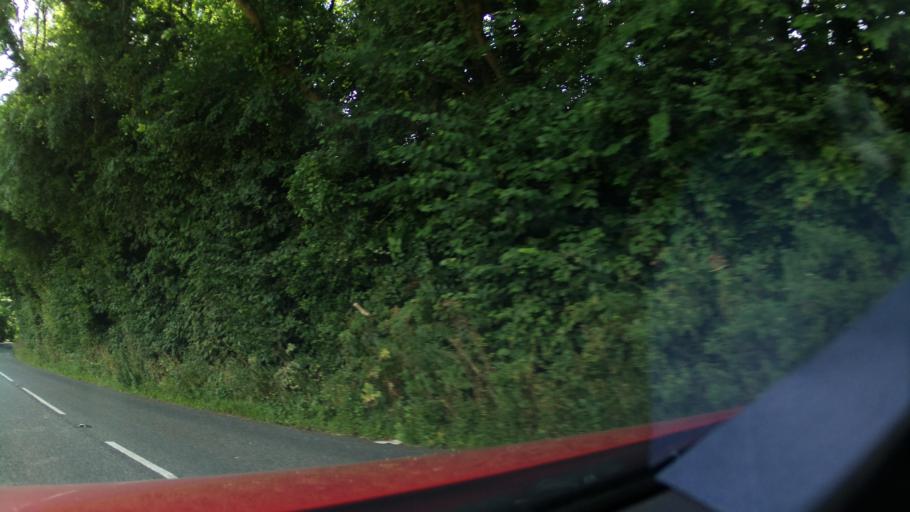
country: GB
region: England
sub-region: Devon
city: Dartmouth
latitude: 50.3604
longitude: -3.5615
